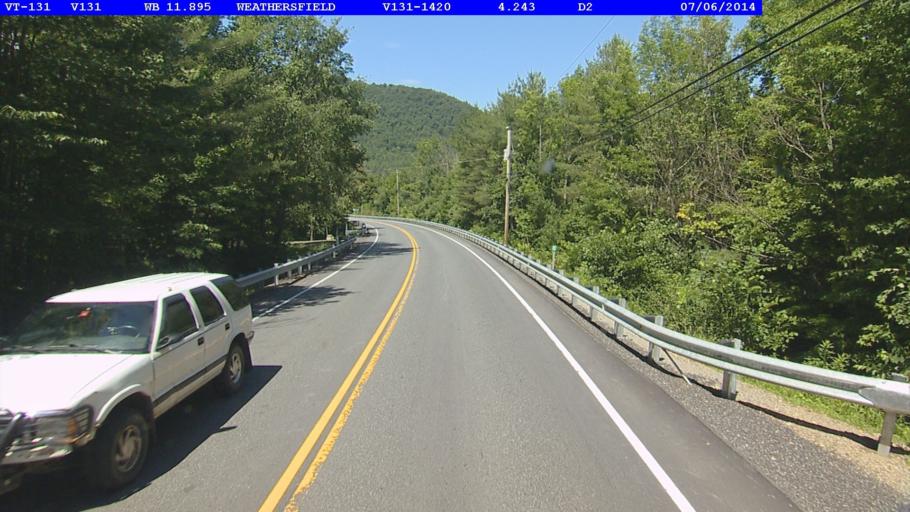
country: US
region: Vermont
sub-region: Windsor County
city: Windsor
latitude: 43.4273
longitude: -72.4811
